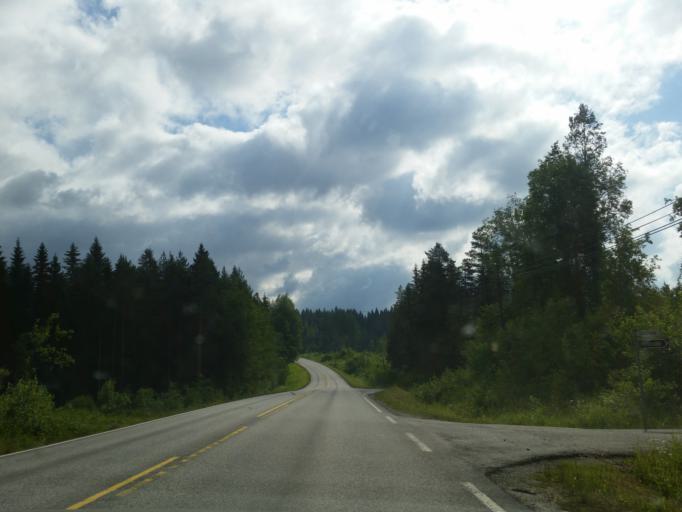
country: FI
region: Northern Savo
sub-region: Kuopio
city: Maaninka
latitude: 62.8447
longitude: 27.3604
